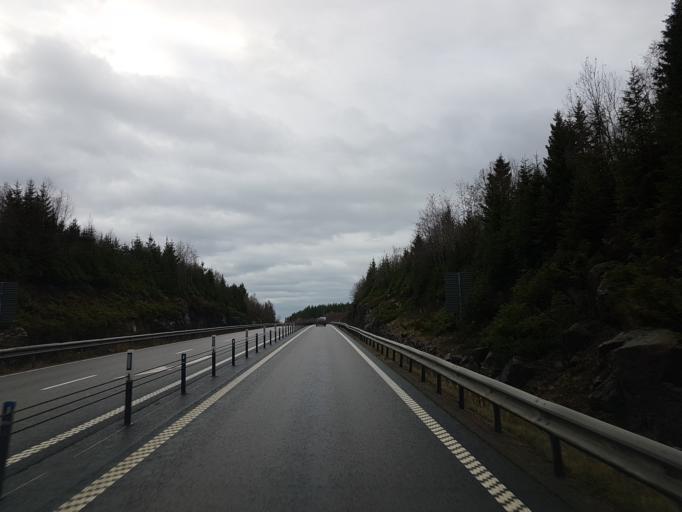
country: SE
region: Gaevleborg
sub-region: Nordanstigs Kommun
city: Bergsjoe
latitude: 62.0693
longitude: 17.2685
